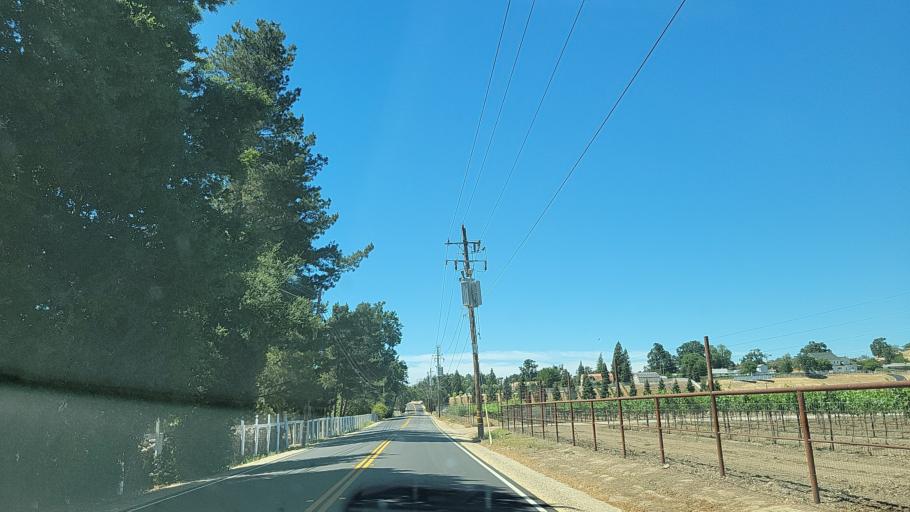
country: US
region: California
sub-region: San Luis Obispo County
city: Atascadero
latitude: 35.4974
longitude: -120.6467
